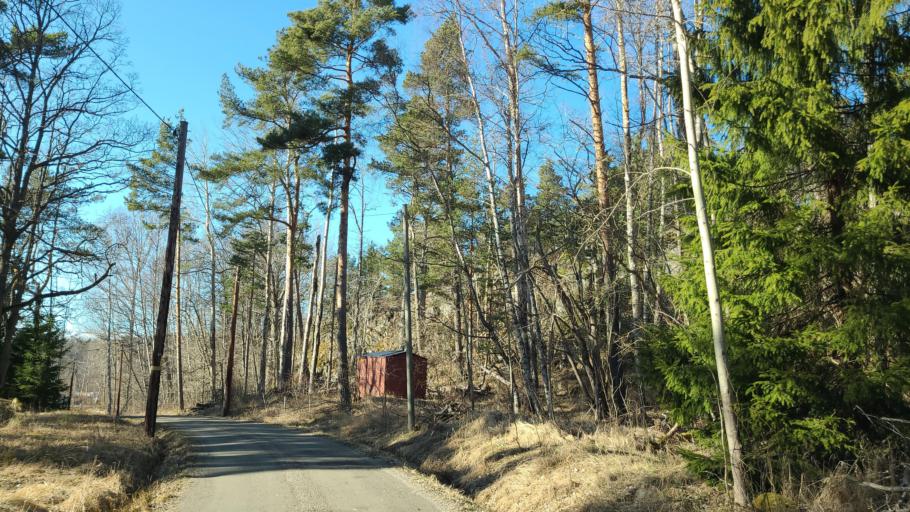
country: SE
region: Stockholm
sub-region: Varmdo Kommun
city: Holo
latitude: 59.3616
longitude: 18.6658
